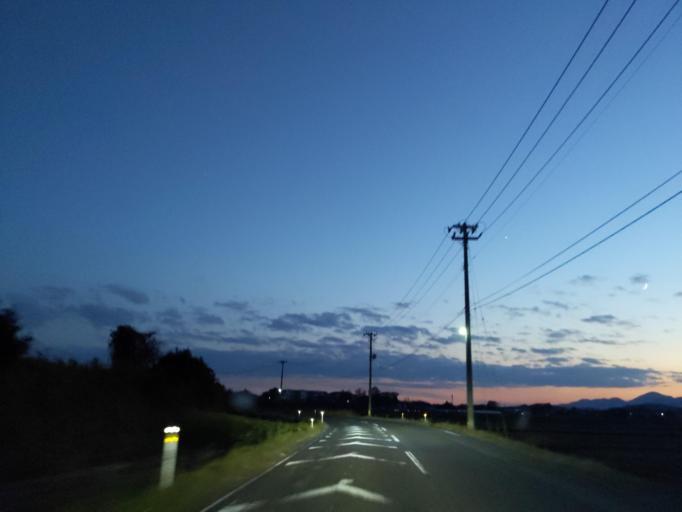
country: JP
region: Fukushima
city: Koriyama
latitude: 37.4274
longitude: 140.3133
